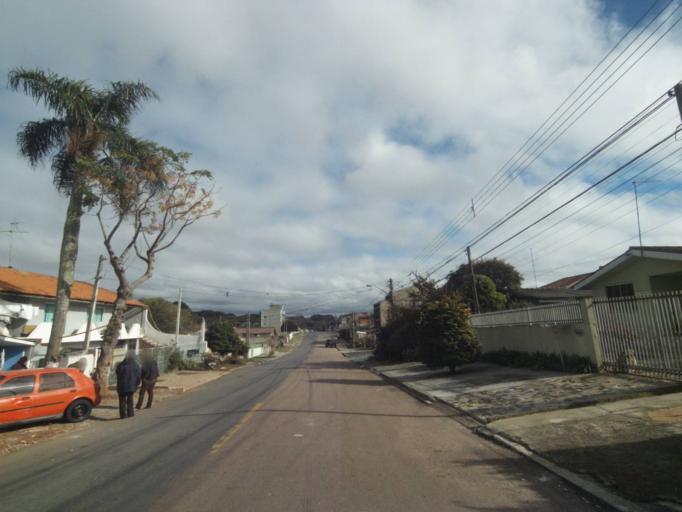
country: BR
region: Parana
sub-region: Sao Jose Dos Pinhais
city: Sao Jose dos Pinhais
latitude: -25.5214
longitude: -49.3064
